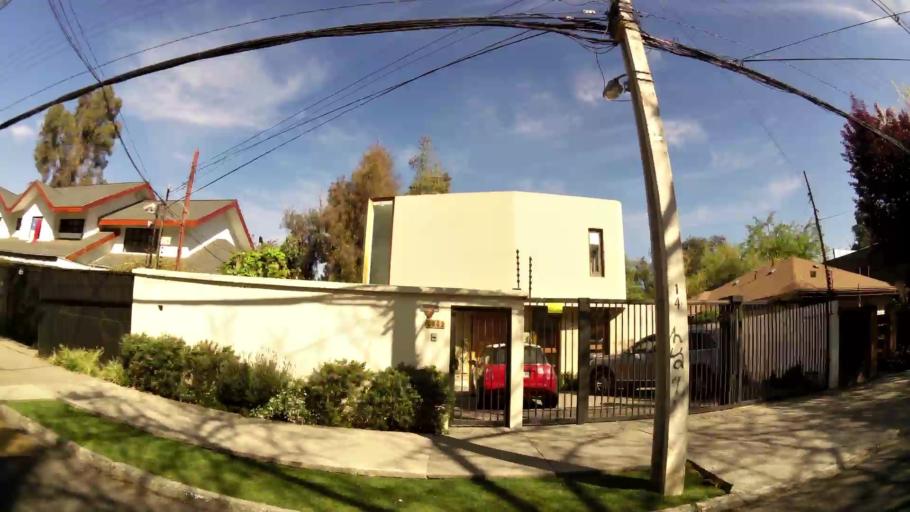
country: CL
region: Santiago Metropolitan
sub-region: Provincia de Santiago
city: Villa Presidente Frei, Nunoa, Santiago, Chile
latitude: -33.4355
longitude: -70.5607
